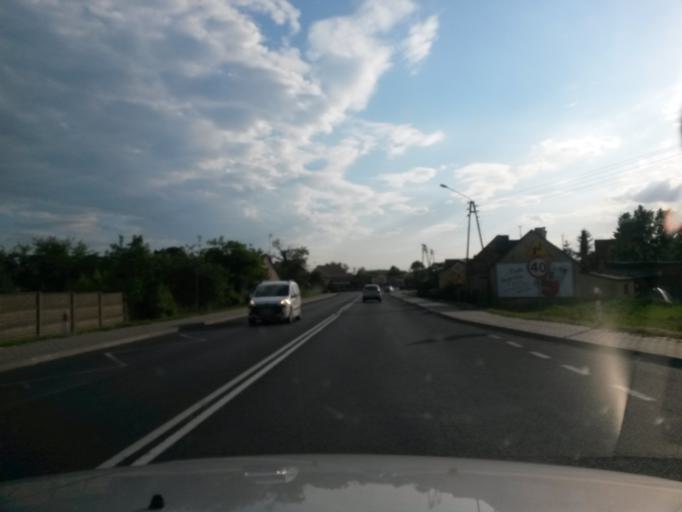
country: PL
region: Lodz Voivodeship
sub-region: Powiat belchatowski
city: Belchatow
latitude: 51.3884
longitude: 19.3909
